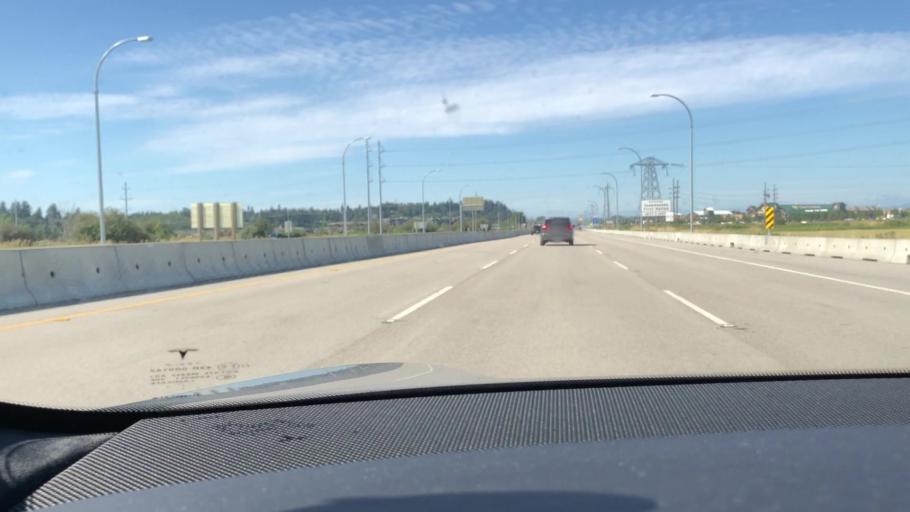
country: CA
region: British Columbia
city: Ladner
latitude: 49.0415
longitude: -123.0716
